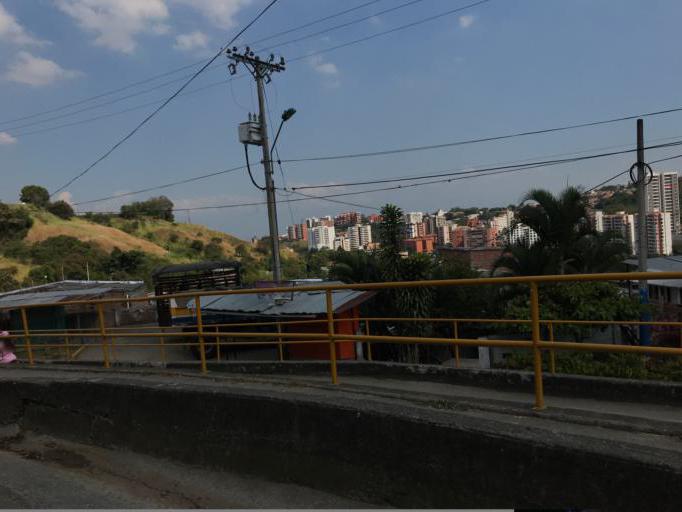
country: CO
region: Valle del Cauca
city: Cali
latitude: 3.4504
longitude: -76.5624
